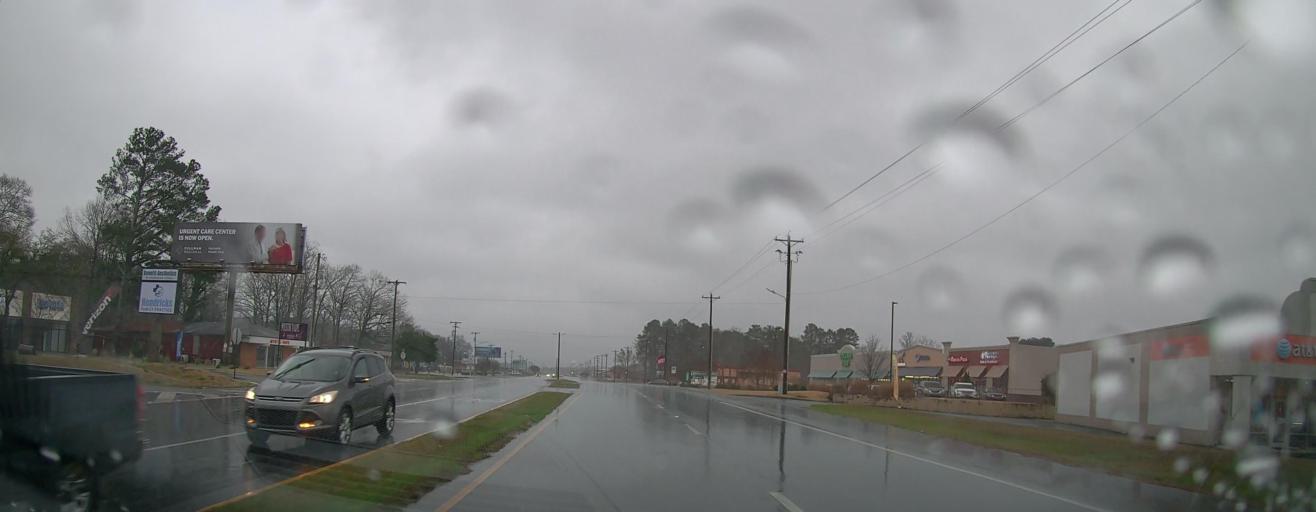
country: US
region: Alabama
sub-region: Morgan County
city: Hartselle
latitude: 34.4531
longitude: -86.9467
